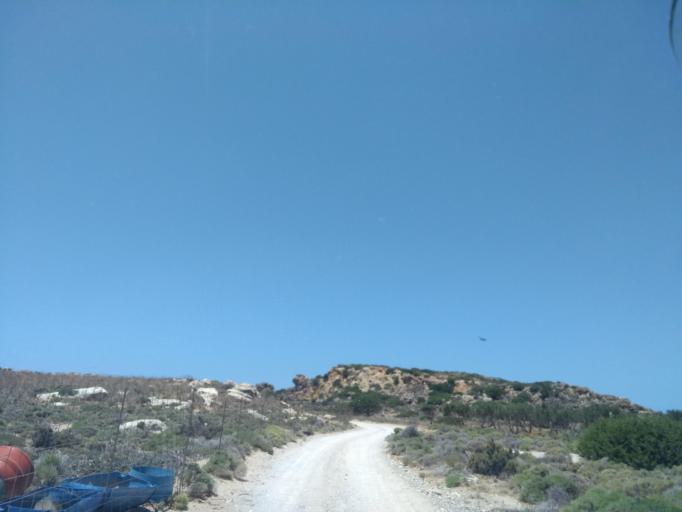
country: GR
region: Crete
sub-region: Nomos Chanias
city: Vryses
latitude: 35.3143
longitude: 23.5356
